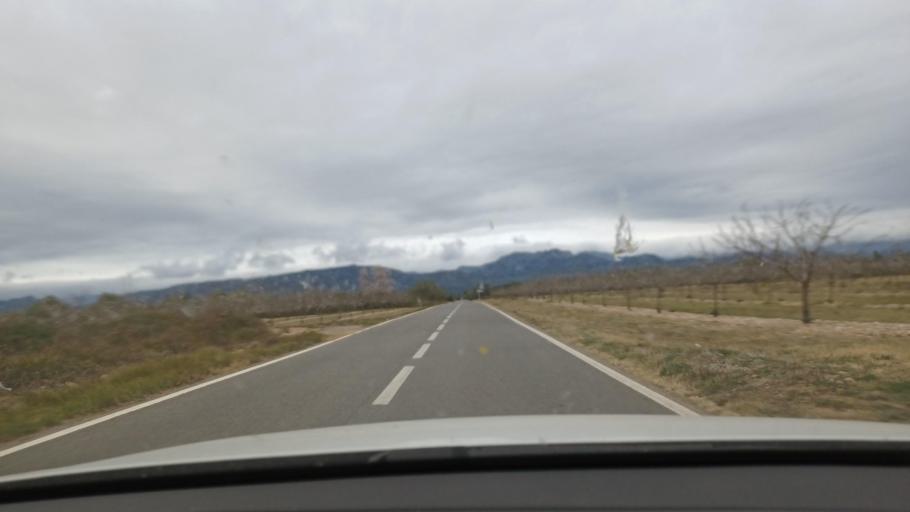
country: ES
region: Catalonia
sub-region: Provincia de Tarragona
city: Ulldecona
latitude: 40.6302
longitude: 0.3626
